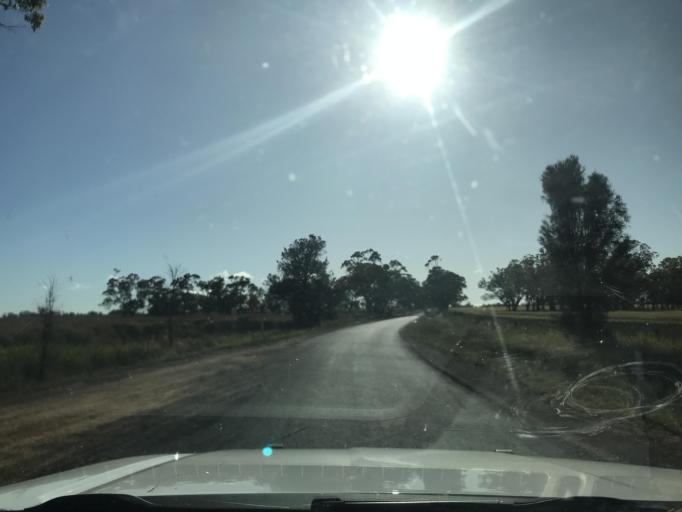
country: AU
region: Victoria
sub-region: Horsham
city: Horsham
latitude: -36.6904
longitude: 141.5272
